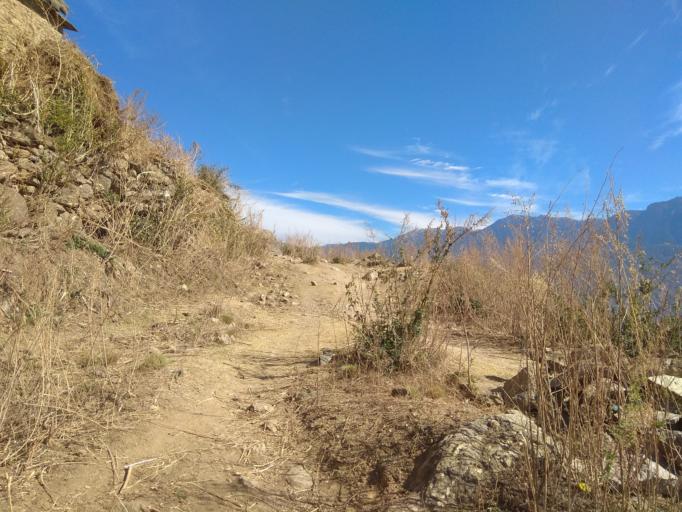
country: NP
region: Mid Western
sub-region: Bheri Zone
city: Dailekh
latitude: 29.2975
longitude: 81.7223
